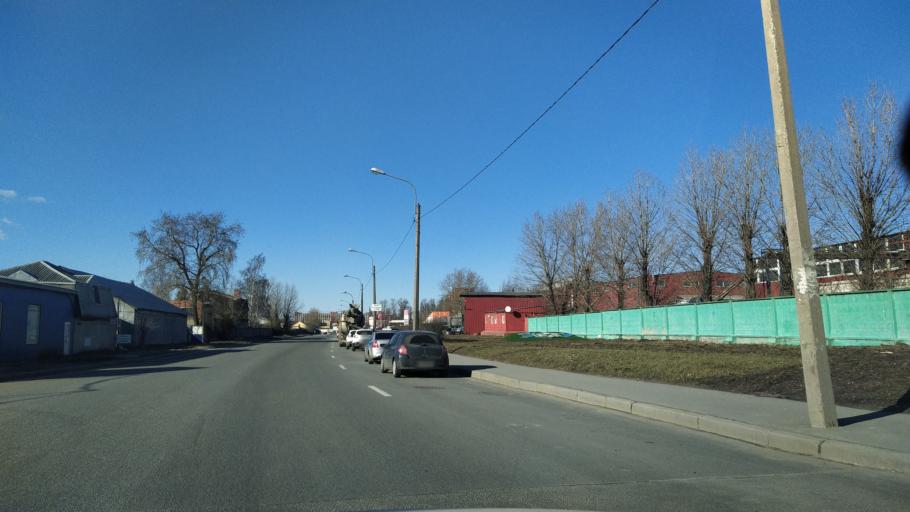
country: RU
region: St.-Petersburg
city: Centralniy
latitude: 59.9069
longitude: 30.3784
